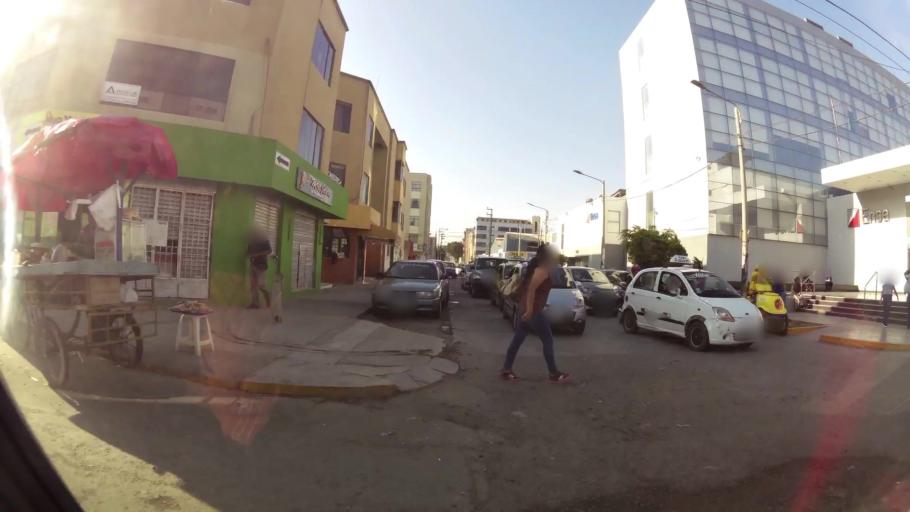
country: PE
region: Lambayeque
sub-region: Provincia de Chiclayo
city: Chiclayo
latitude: -6.7706
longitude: -79.8440
